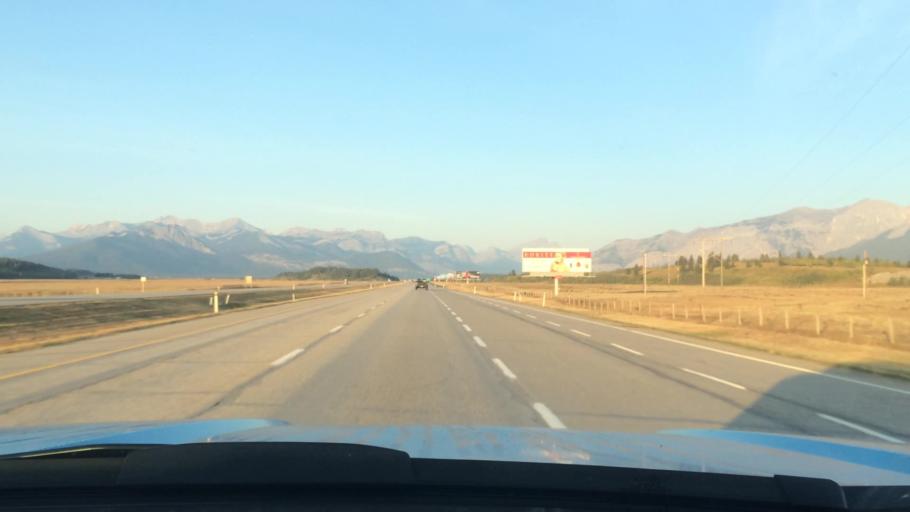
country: CA
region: Alberta
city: Canmore
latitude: 51.1228
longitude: -114.9736
